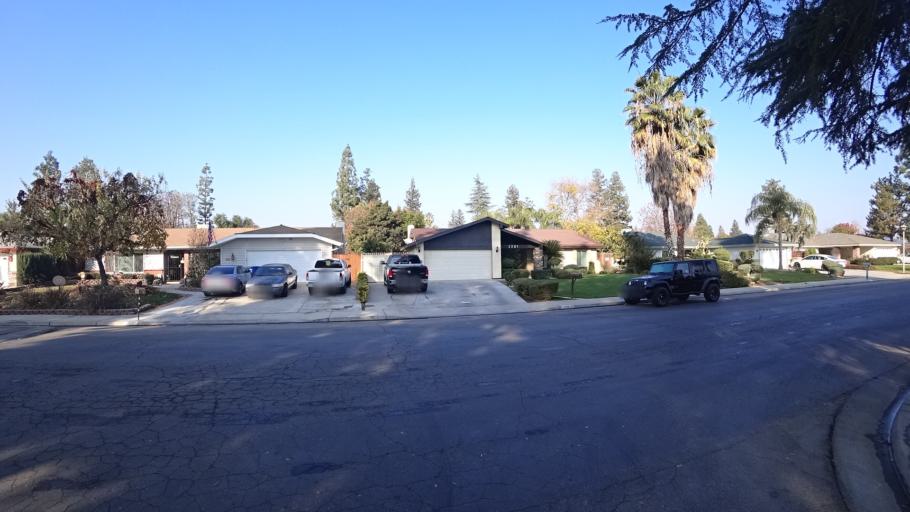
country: US
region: California
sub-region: Kern County
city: Greenacres
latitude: 35.3389
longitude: -119.0840
